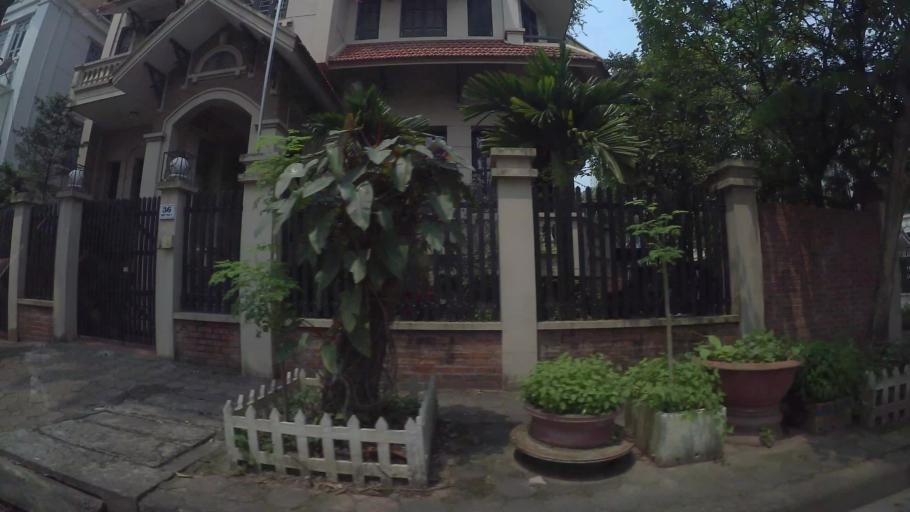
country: VN
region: Ha Noi
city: Van Dien
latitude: 20.9637
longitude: 105.8346
